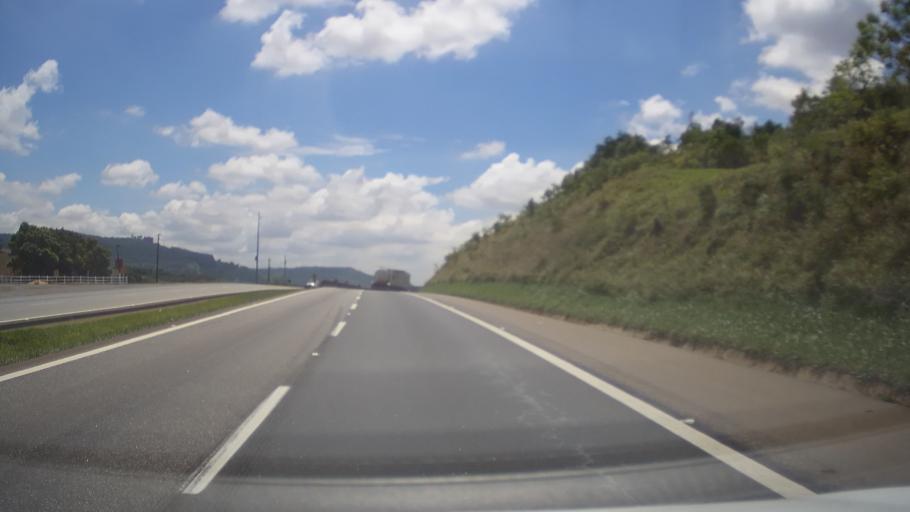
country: BR
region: Minas Gerais
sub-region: Campanha
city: Campanha
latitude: -21.8351
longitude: -45.5038
